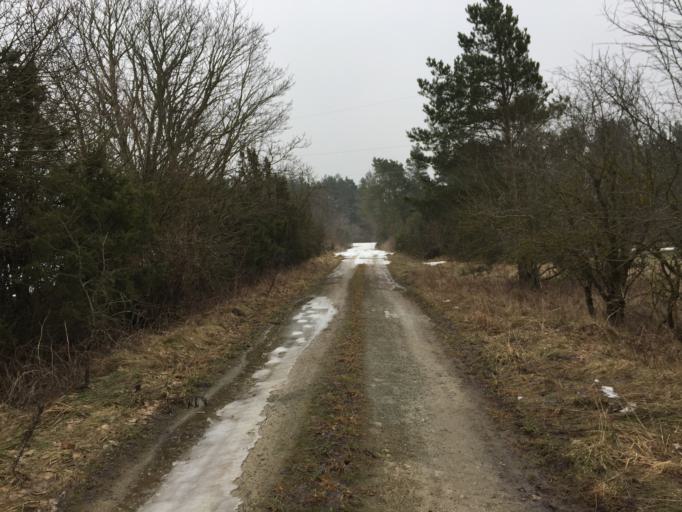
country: EE
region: Saare
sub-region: Orissaare vald
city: Orissaare
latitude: 58.4173
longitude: 22.8227
